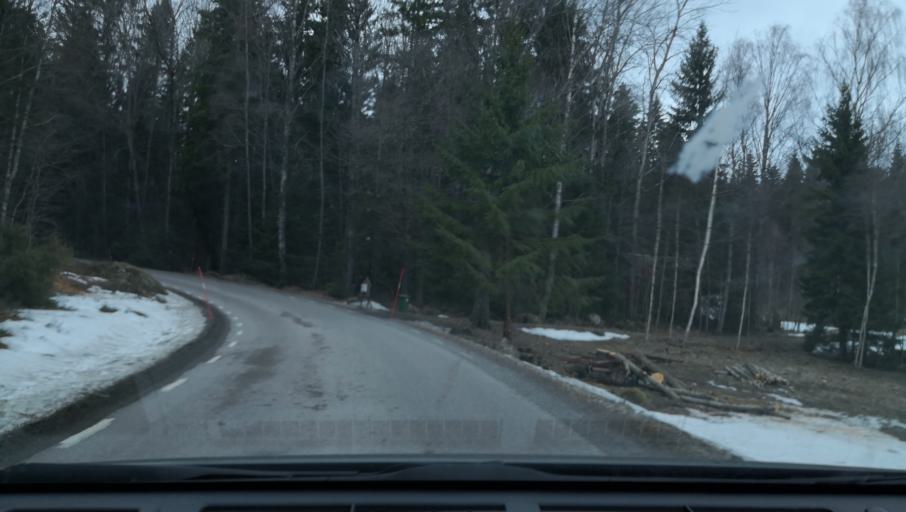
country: SE
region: Vaestmanland
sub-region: Kopings Kommun
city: Kolsva
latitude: 59.5702
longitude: 15.7244
